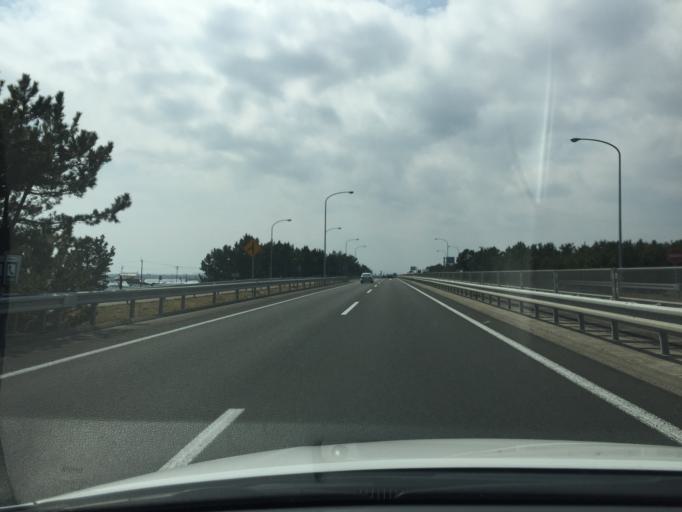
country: JP
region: Miyagi
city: Sendai
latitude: 38.1823
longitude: 140.9320
